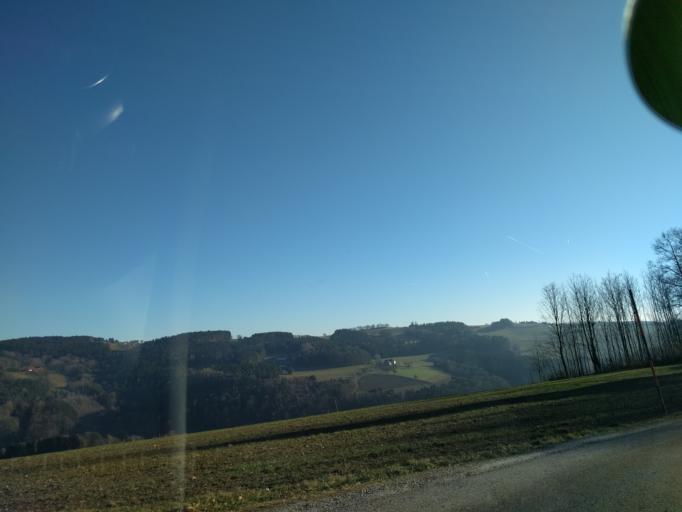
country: AT
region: Upper Austria
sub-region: Politischer Bezirk Urfahr-Umgebung
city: Kirchschlag bei Linz
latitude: 48.3998
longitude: 14.2861
